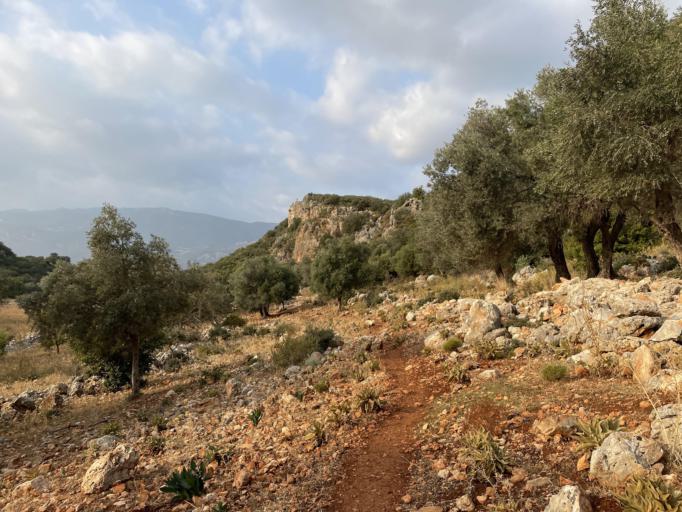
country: TR
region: Antalya
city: Kas
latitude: 36.1679
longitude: 29.6533
